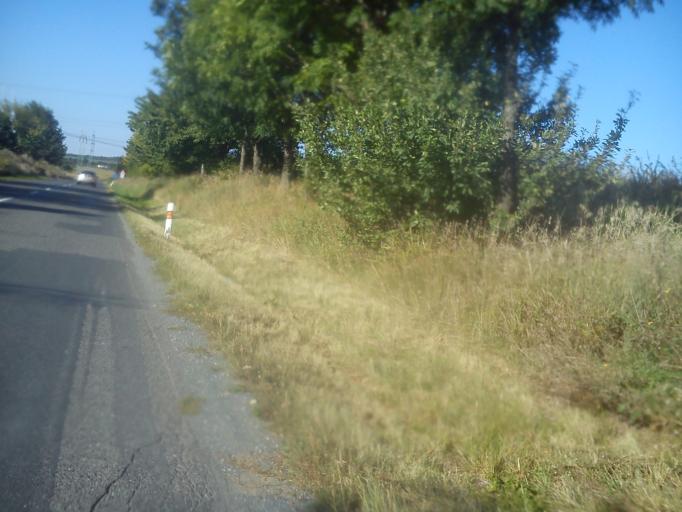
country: CZ
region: South Moravian
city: Telnice
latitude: 49.0957
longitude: 16.7413
